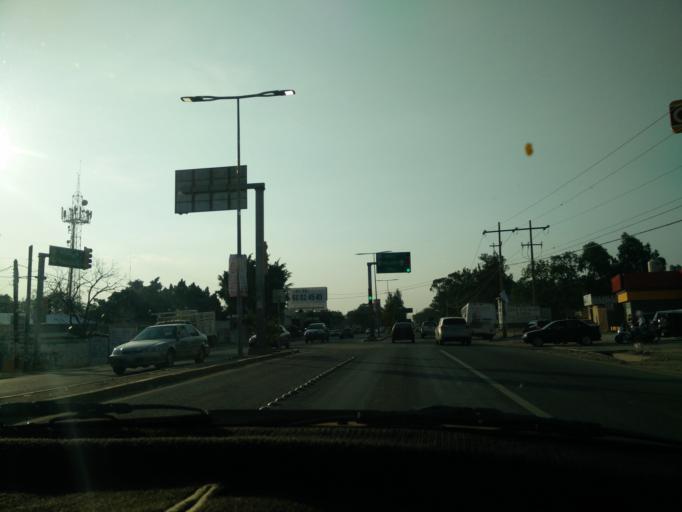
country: MX
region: Oaxaca
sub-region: Santa Maria Atzompa
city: San Jeronimo Yahuiche
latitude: 17.1158
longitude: -96.7588
